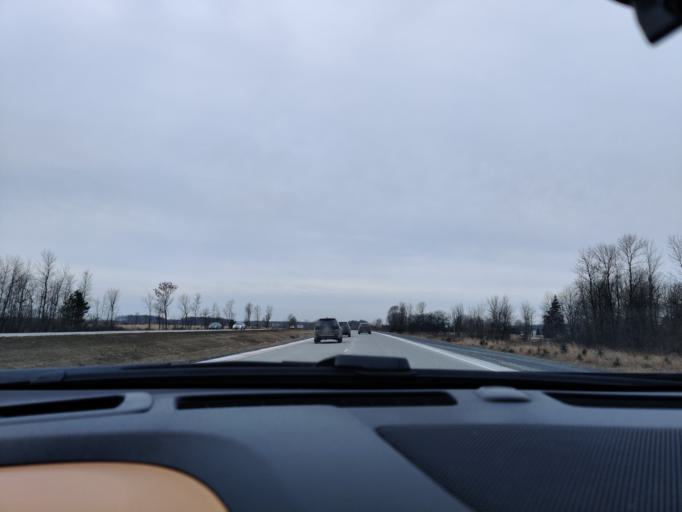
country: US
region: New York
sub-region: St. Lawrence County
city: Massena
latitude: 45.0435
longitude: -74.9167
